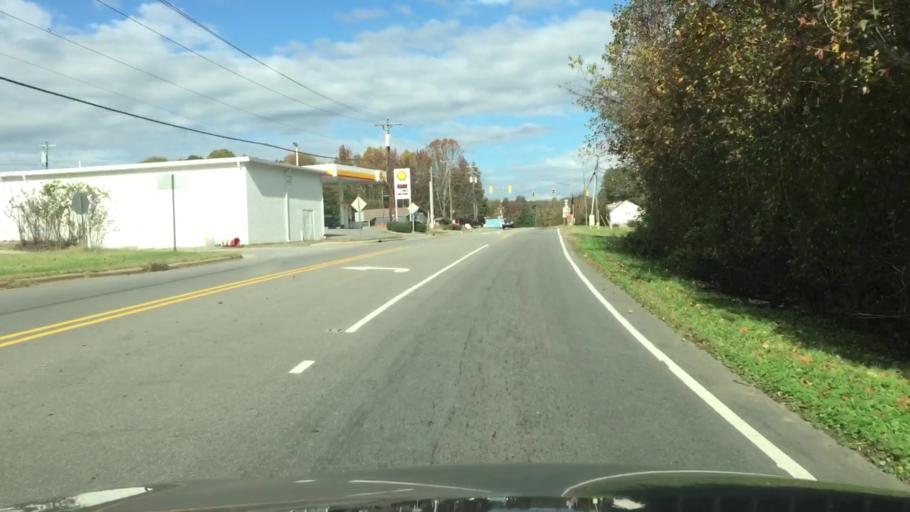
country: US
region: North Carolina
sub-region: Iredell County
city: Mooresville
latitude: 35.6221
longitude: -80.8260
